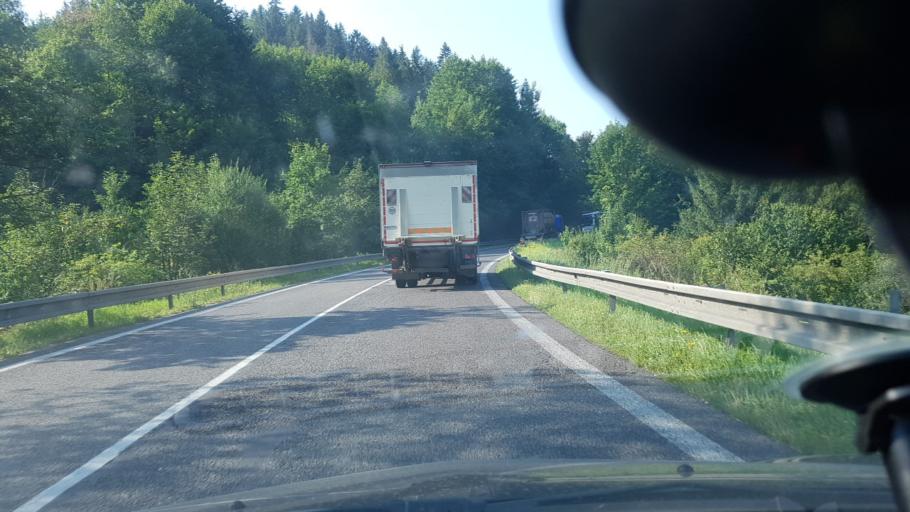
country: SK
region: Zilinsky
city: Tvrdosin
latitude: 49.2895
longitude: 19.4941
